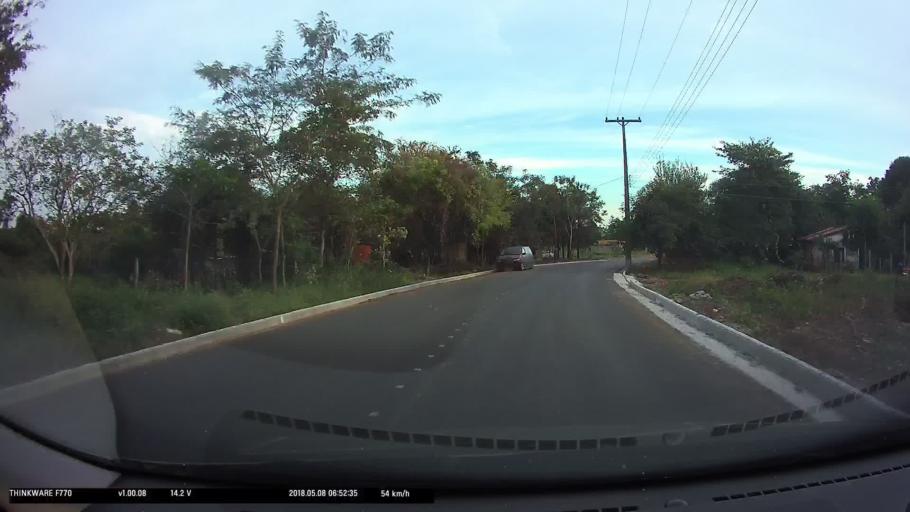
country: PY
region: Central
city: Limpio
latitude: -25.2355
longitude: -57.4669
